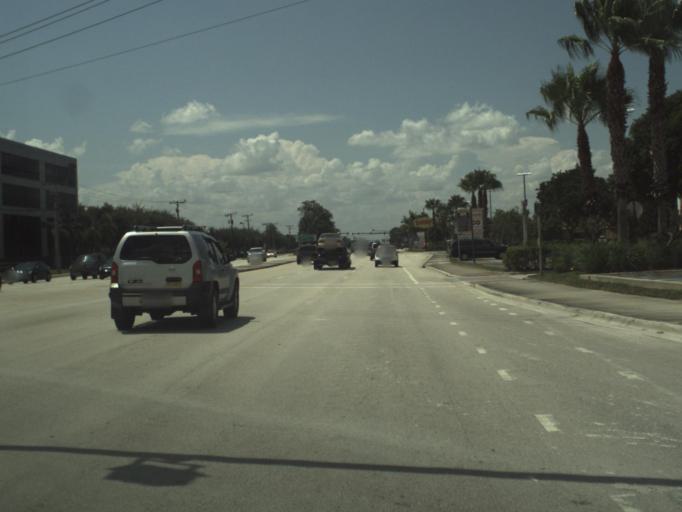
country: US
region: Florida
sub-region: Martin County
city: Stuart
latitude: 27.1755
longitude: -80.2342
